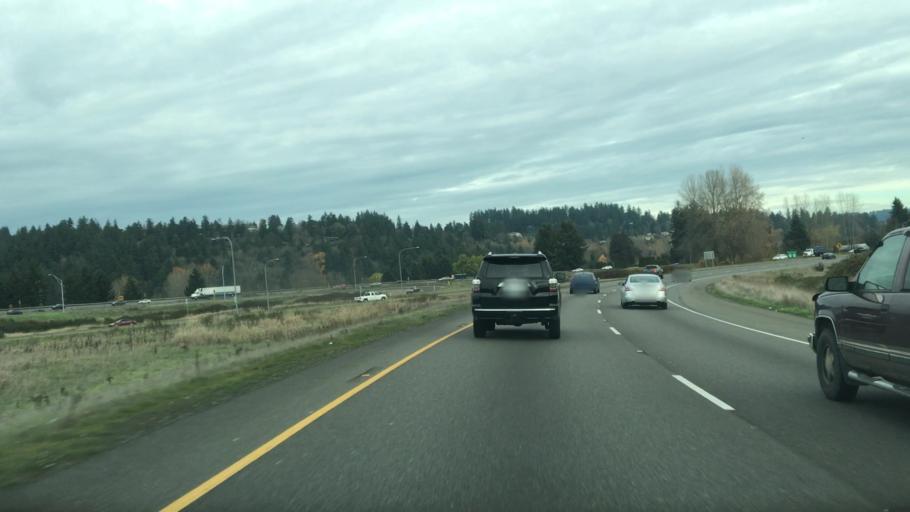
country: US
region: Washington
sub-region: Pierce County
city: North Puyallup
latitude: 47.2012
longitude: -122.2783
